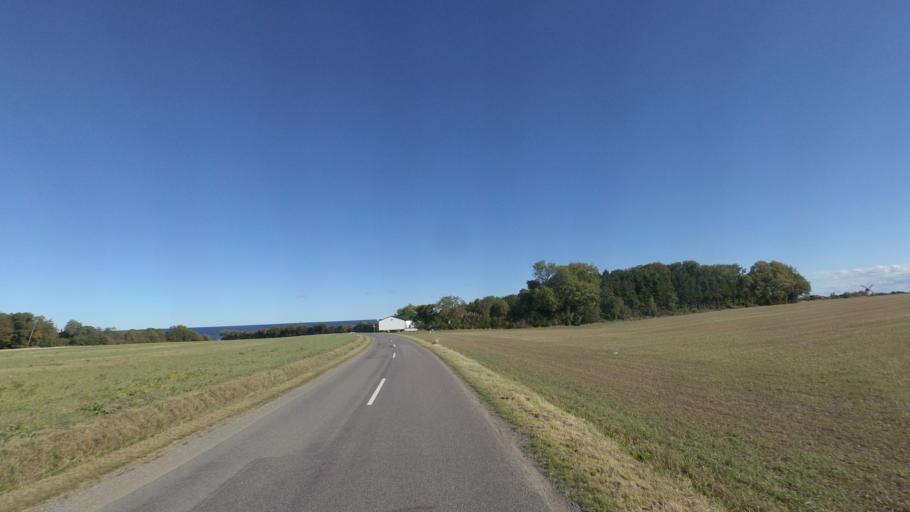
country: DK
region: Capital Region
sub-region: Bornholm Kommune
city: Nexo
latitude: 55.1102
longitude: 15.1354
